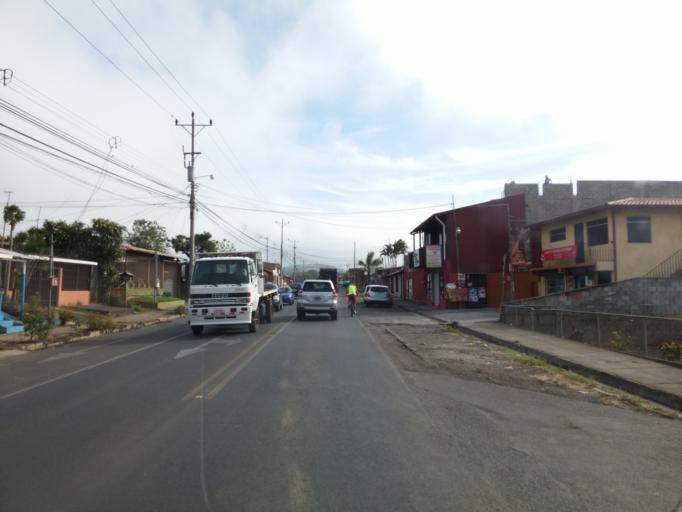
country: CR
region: Alajuela
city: San Ramon
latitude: 10.0998
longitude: -84.4681
